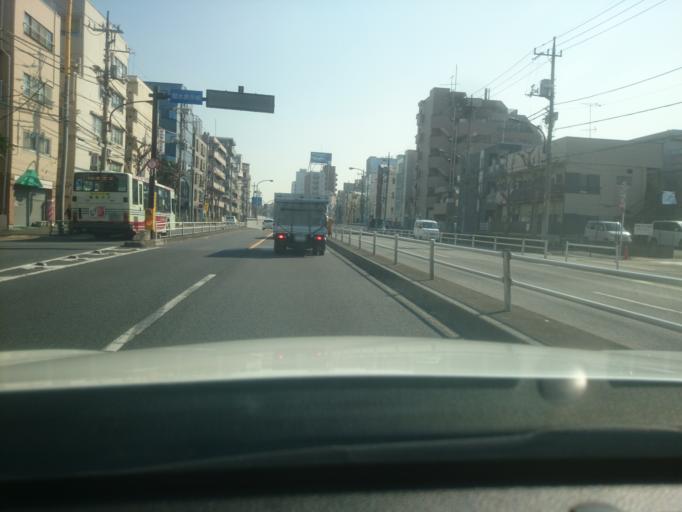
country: JP
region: Tokyo
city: Musashino
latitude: 35.7103
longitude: 139.6148
